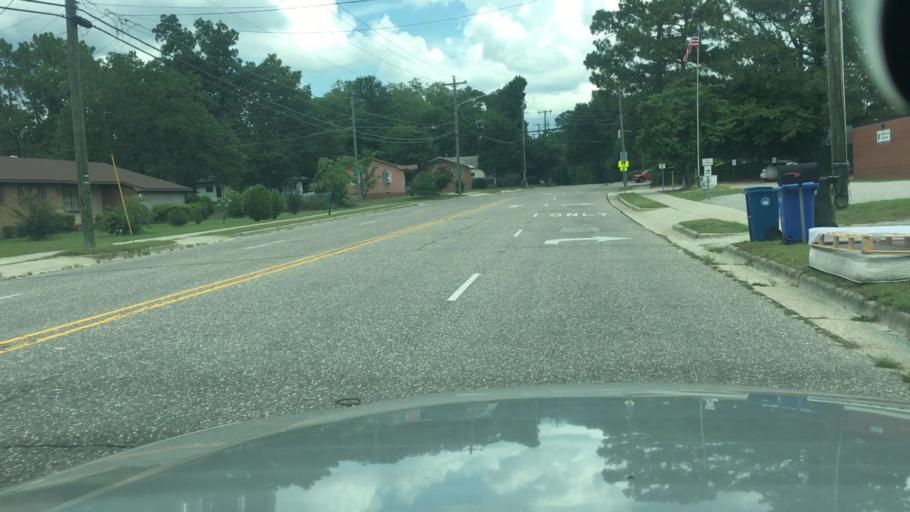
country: US
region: North Carolina
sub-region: Cumberland County
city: Fayetteville
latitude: 35.0871
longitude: -78.9003
